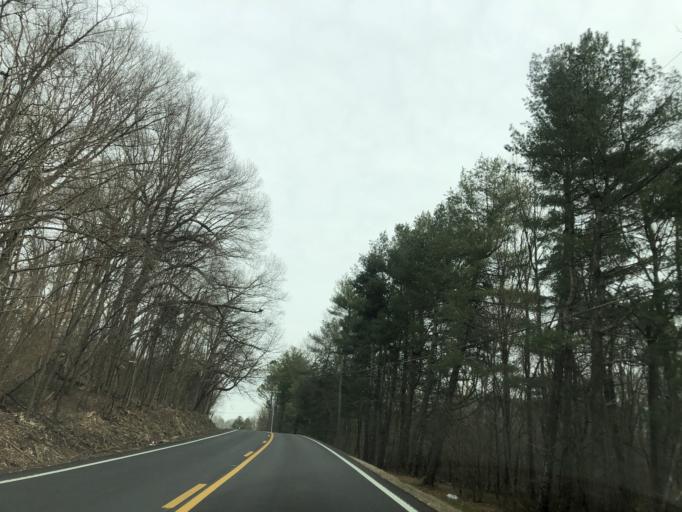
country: US
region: Tennessee
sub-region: Robertson County
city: Greenbrier
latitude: 36.4742
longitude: -86.7557
